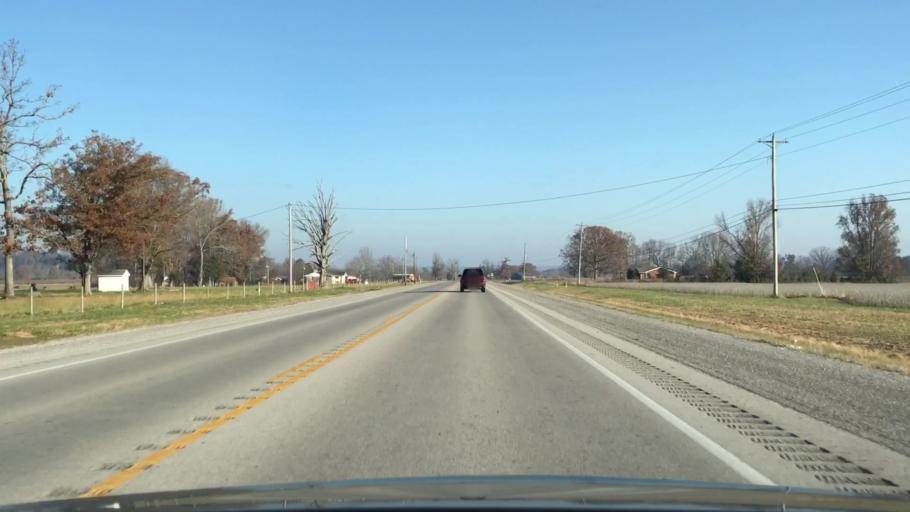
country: US
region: Kentucky
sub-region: Edmonson County
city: Brownsville
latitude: 37.1374
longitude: -86.2316
